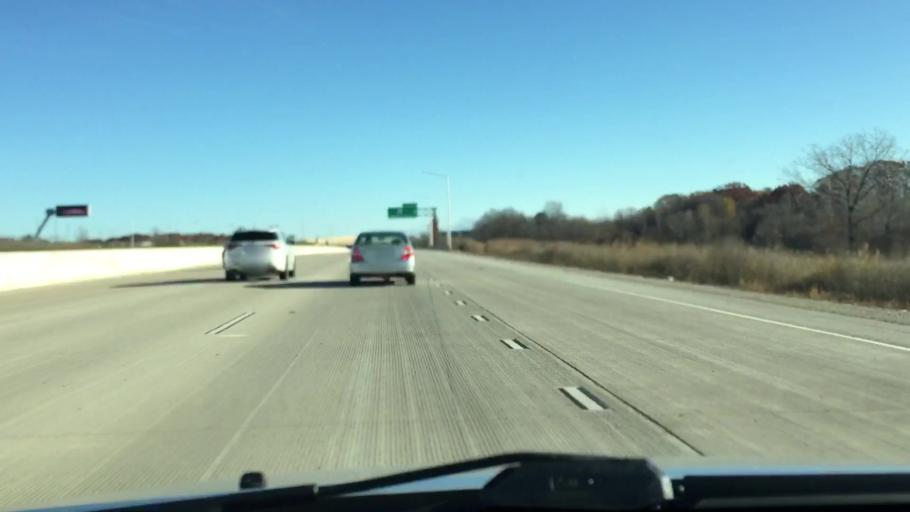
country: US
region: Wisconsin
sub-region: Brown County
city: De Pere
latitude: 44.4270
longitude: -88.1177
